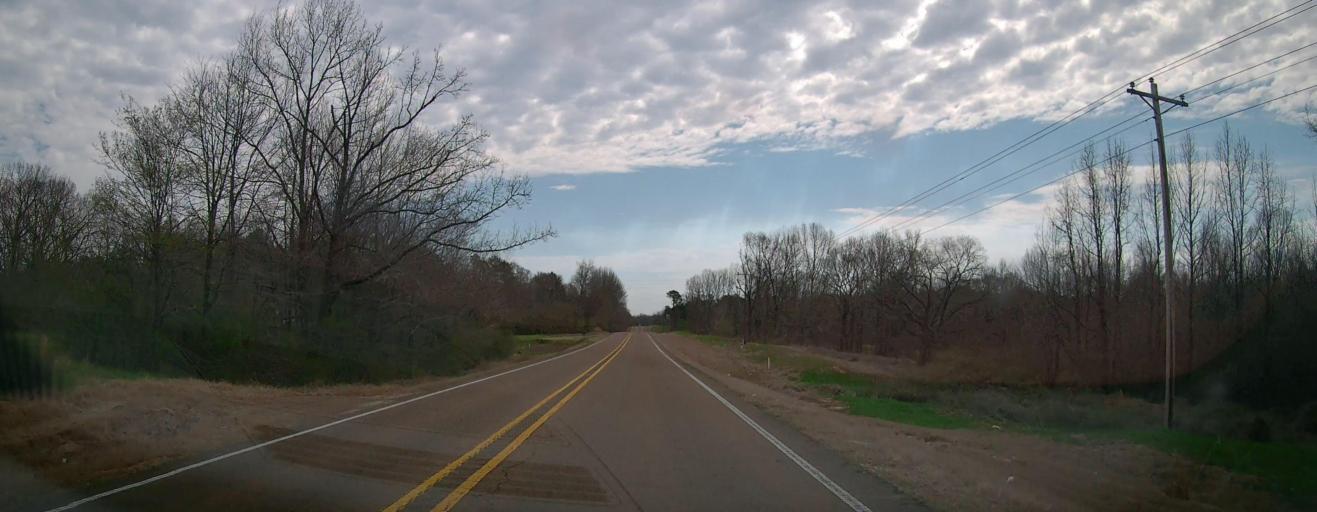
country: US
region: Mississippi
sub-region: Marshall County
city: Byhalia
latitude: 34.8534
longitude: -89.6380
